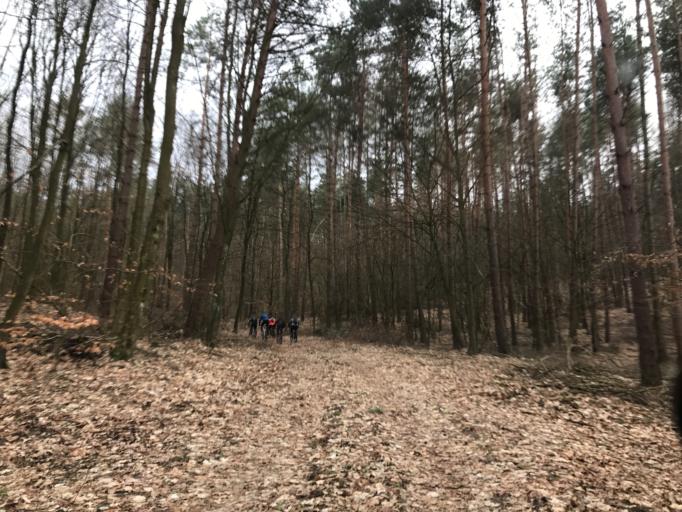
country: PL
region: Kujawsko-Pomorskie
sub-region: Powiat brodnicki
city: Gorzno
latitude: 53.2018
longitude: 19.6690
